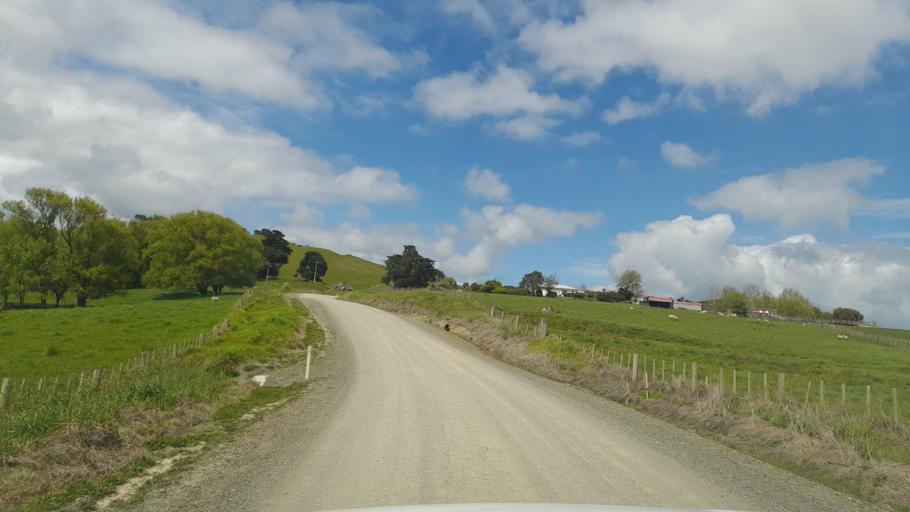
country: NZ
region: Auckland
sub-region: Auckland
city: Wellsford
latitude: -36.1794
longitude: 174.3154
